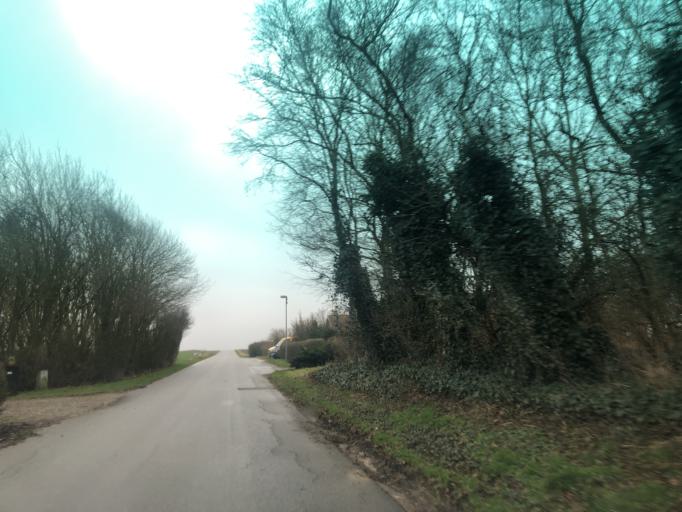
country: DK
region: Central Jutland
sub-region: Struer Kommune
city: Struer
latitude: 56.4467
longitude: 8.5883
